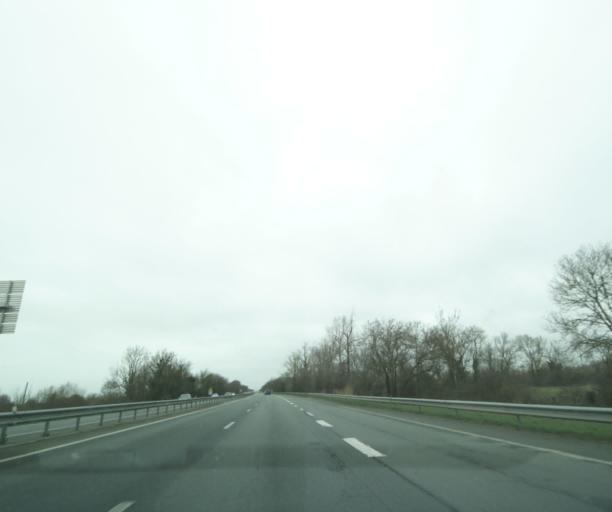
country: FR
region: Poitou-Charentes
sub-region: Departement de la Charente-Maritime
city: Chatelaillon-Plage
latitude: 46.0831
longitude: -1.0784
